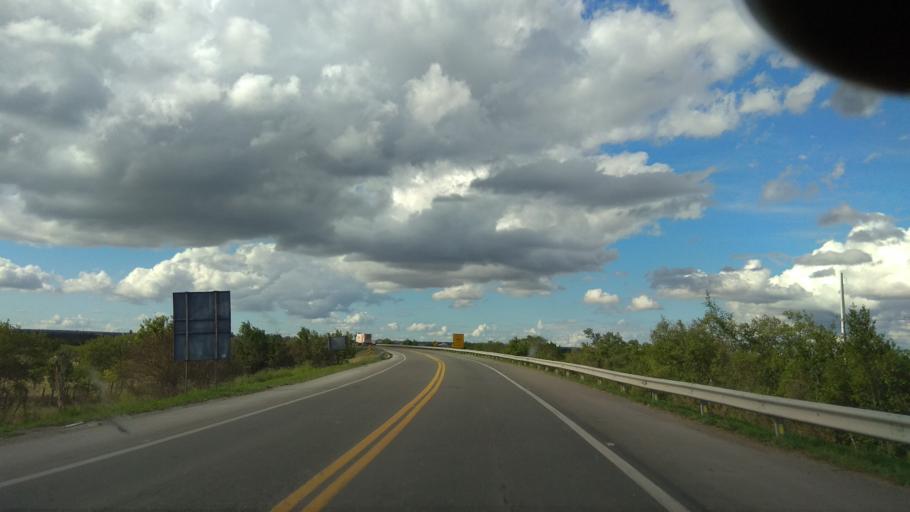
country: BR
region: Bahia
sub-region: Castro Alves
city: Castro Alves
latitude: -12.5913
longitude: -39.5260
